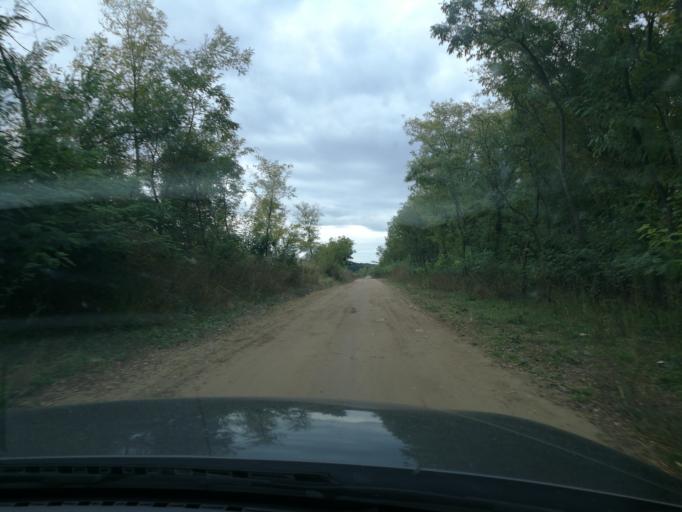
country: HU
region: Szabolcs-Szatmar-Bereg
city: Nyirpazony
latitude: 47.9877
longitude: 21.7888
